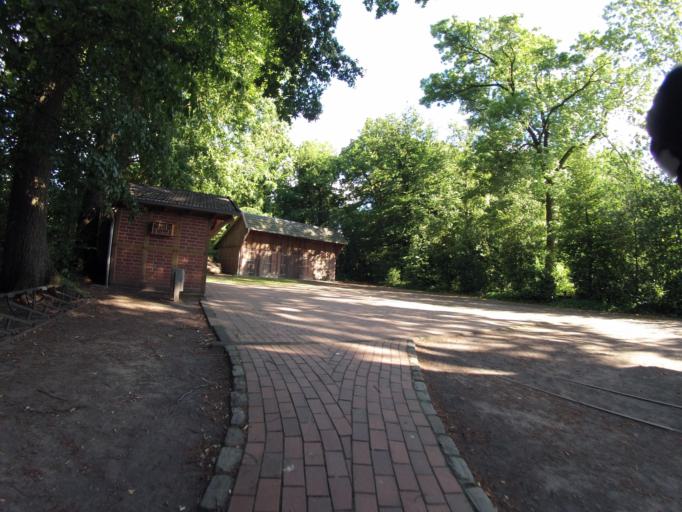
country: DE
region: North Rhine-Westphalia
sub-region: Regierungsbezirk Munster
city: Horstel
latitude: 52.3107
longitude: 7.5974
